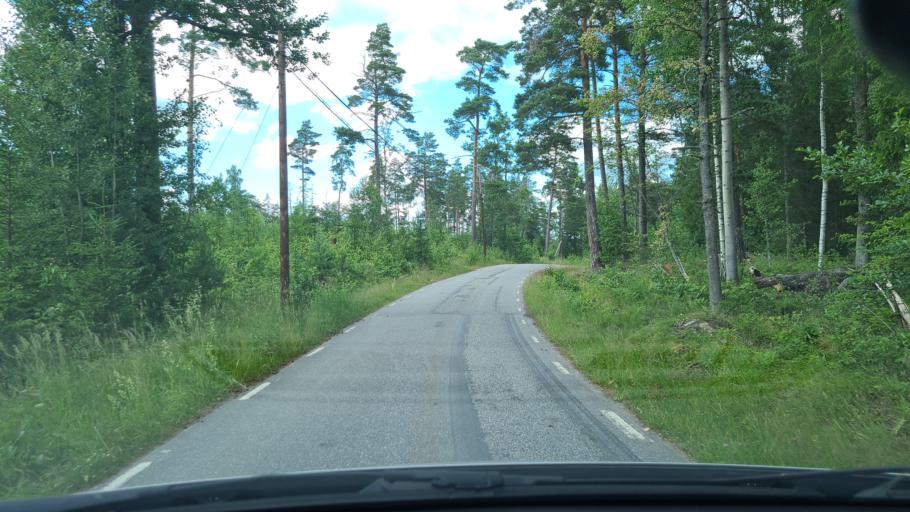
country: SE
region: Stockholm
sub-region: Vaxholms Kommun
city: Vaxholm
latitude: 59.4183
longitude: 18.4327
